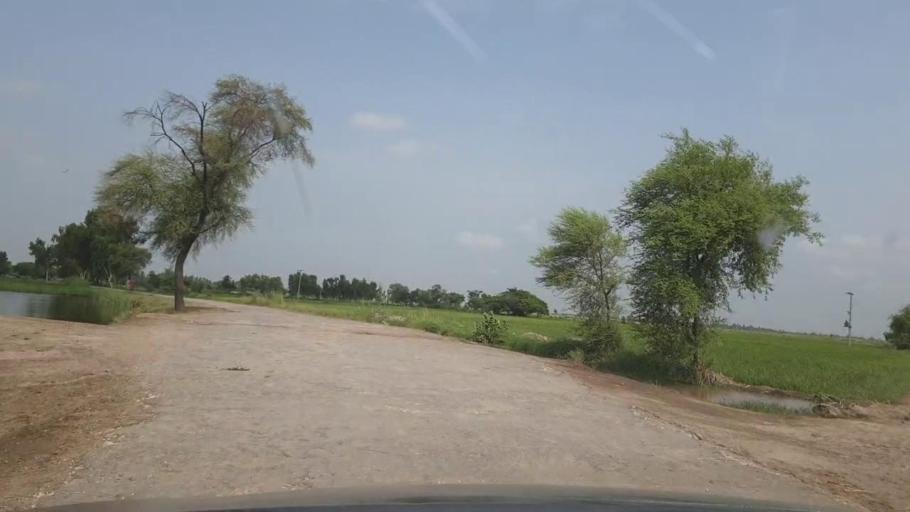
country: PK
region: Sindh
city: Ratodero
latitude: 27.8560
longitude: 68.2990
